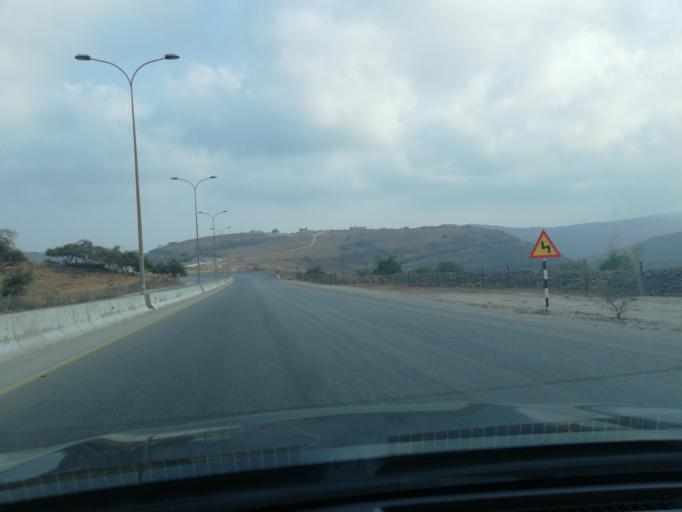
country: OM
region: Zufar
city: Salalah
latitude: 17.1666
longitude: 54.1245
